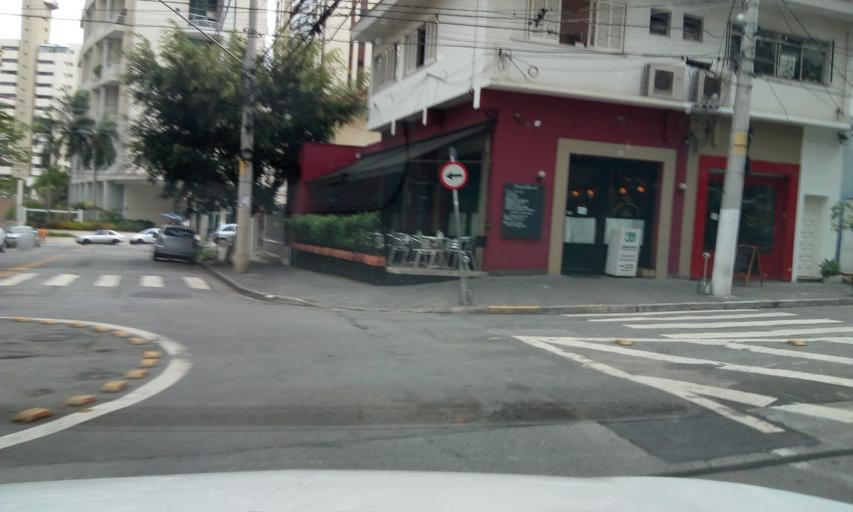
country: BR
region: Sao Paulo
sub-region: Sao Paulo
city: Sao Paulo
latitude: -23.6004
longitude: -46.6689
